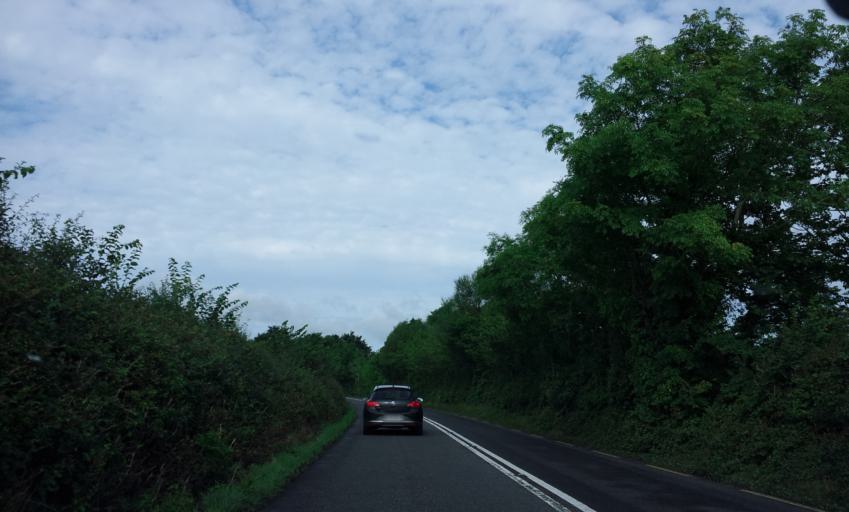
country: IE
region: Munster
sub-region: Ciarrai
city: Killorglin
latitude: 52.1005
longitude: -9.7110
